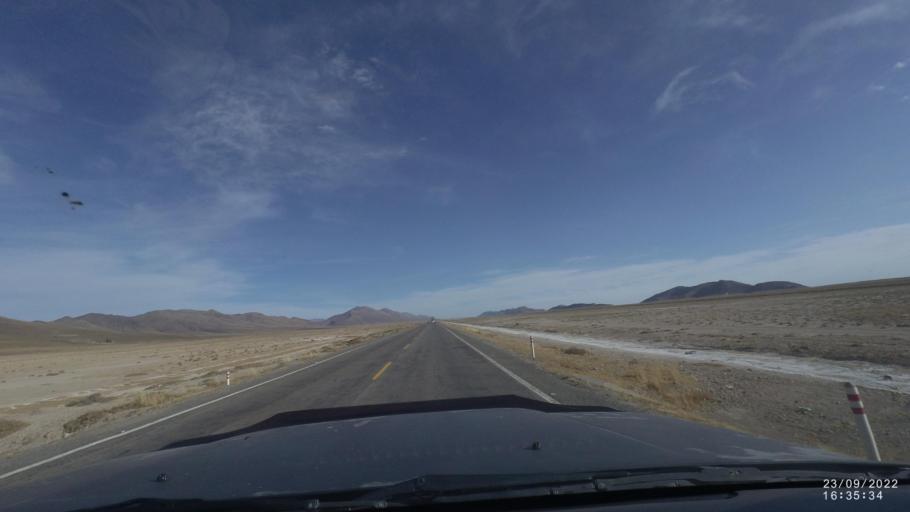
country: BO
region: Oruro
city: Machacamarca
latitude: -18.2064
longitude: -67.0107
